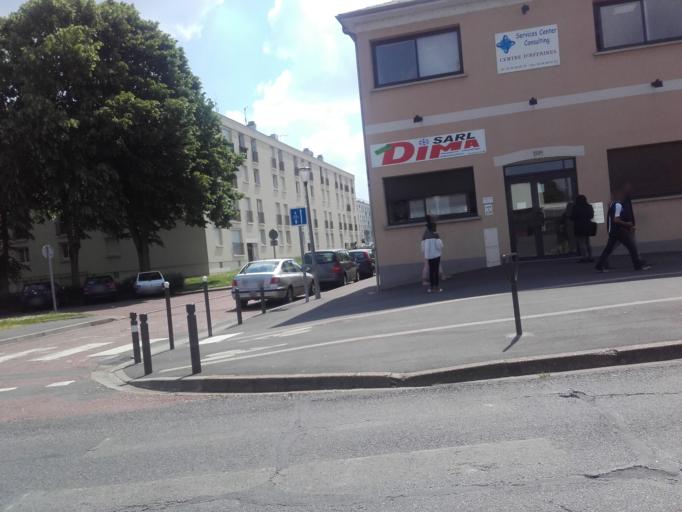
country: FR
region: Centre
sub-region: Departement du Loir-et-Cher
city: Blois
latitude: 47.5933
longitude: 1.3117
